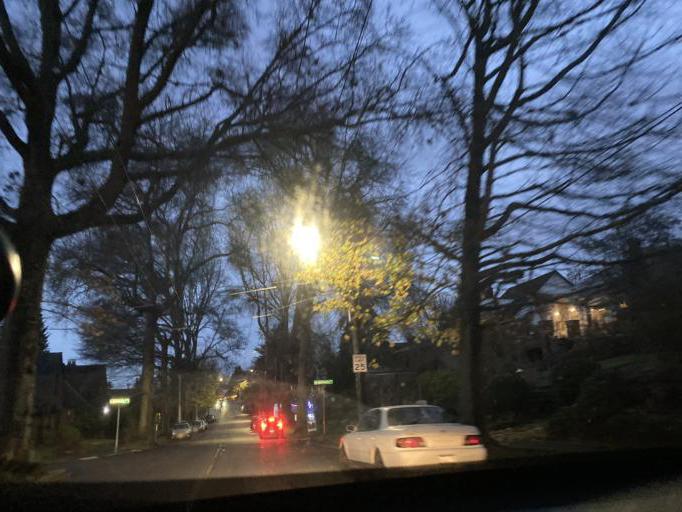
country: US
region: Washington
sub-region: King County
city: Seattle
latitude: 47.6433
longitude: -122.3702
